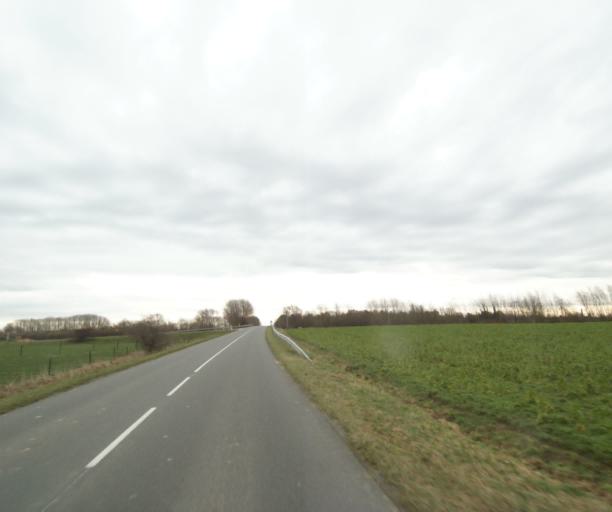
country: FR
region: Nord-Pas-de-Calais
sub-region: Departement du Nord
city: Saultain
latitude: 50.3594
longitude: 3.5839
